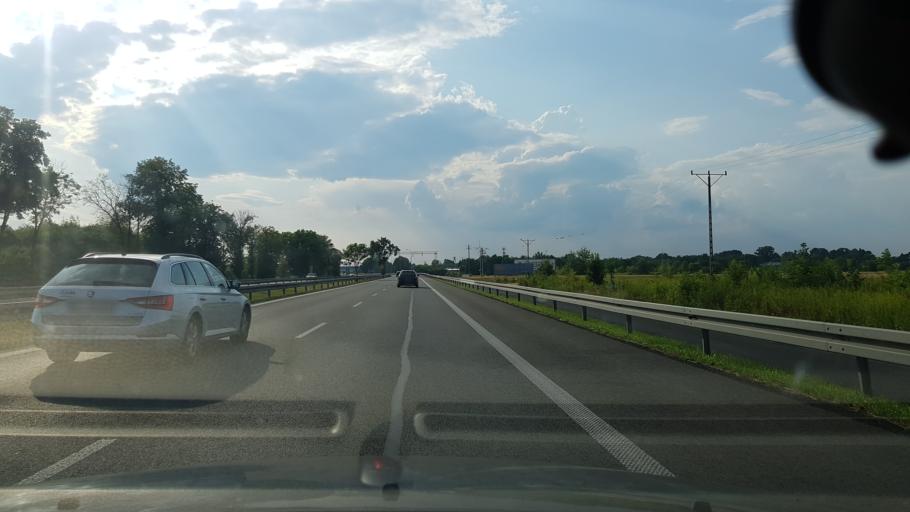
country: PL
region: Masovian Voivodeship
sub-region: Powiat nowodworski
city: Nowy Dwor Mazowiecki
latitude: 52.3854
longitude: 20.7489
